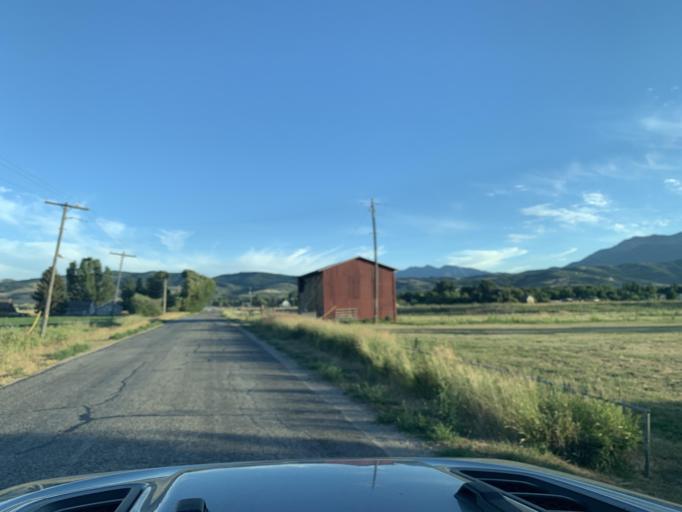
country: US
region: Utah
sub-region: Weber County
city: Wolf Creek
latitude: 41.2683
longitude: -111.7617
